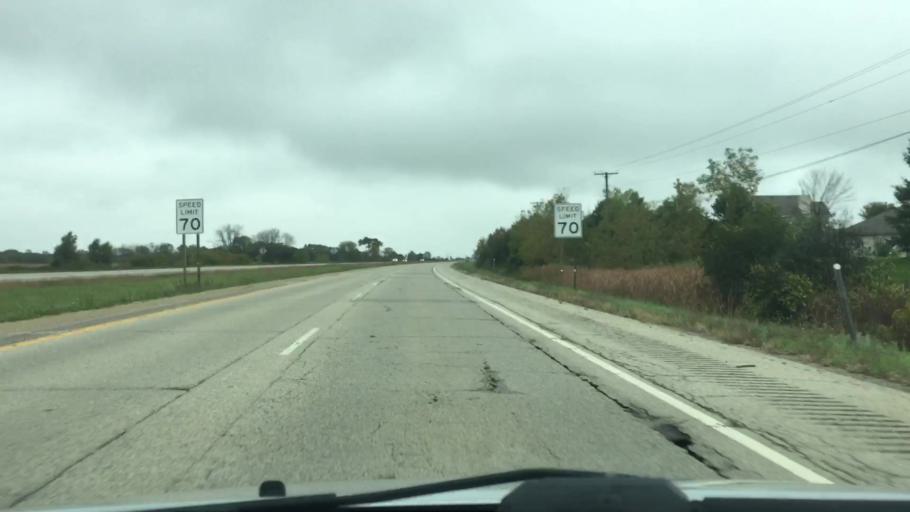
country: US
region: Wisconsin
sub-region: Walworth County
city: Elkhorn
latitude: 42.6915
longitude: -88.5350
